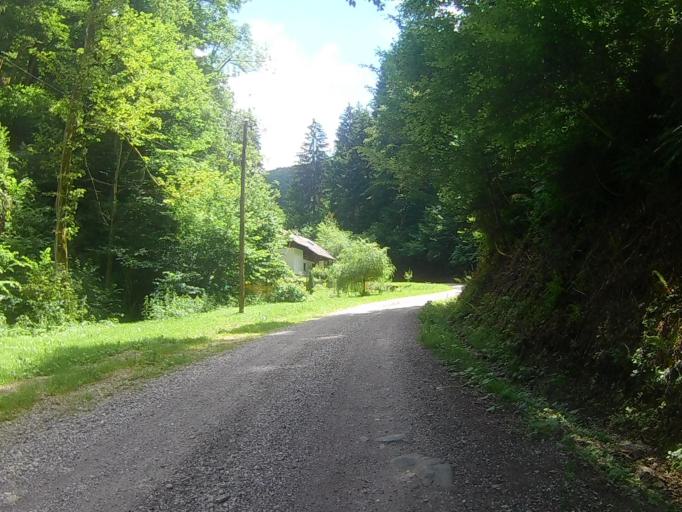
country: SI
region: Ruse
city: Ruse
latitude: 46.5292
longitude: 15.5001
